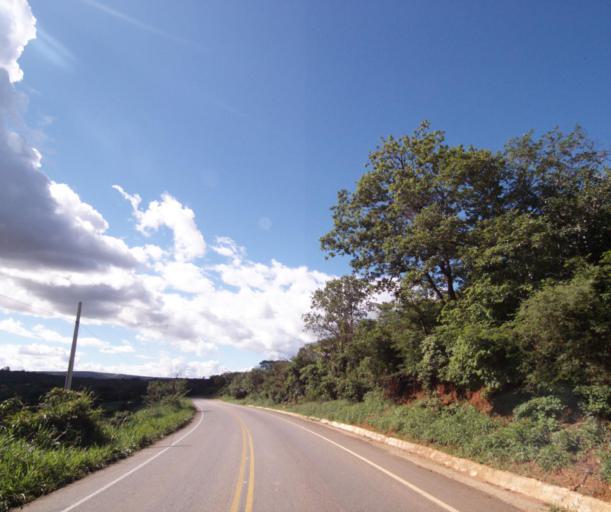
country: BR
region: Bahia
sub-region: Caetite
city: Caetite
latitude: -14.0734
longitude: -42.4576
